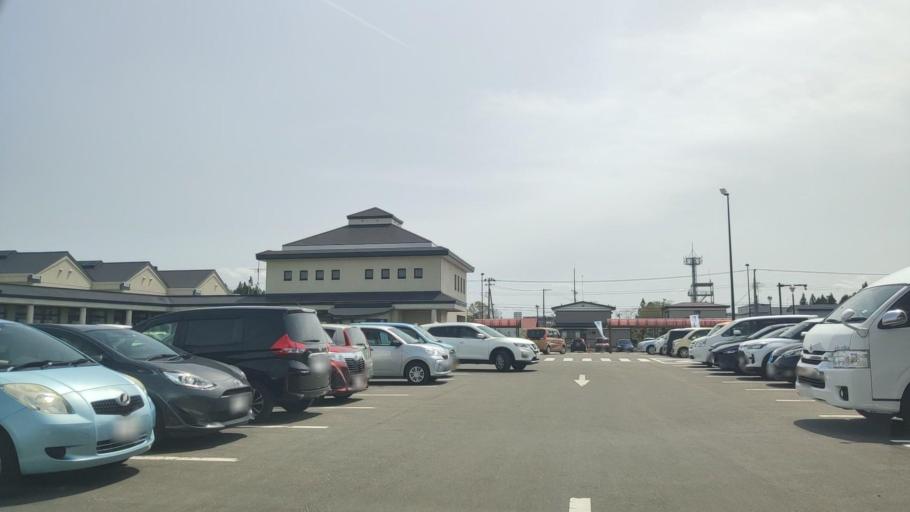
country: JP
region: Aomori
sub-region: Misawa Shi
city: Inuotose
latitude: 40.7172
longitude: 141.1556
